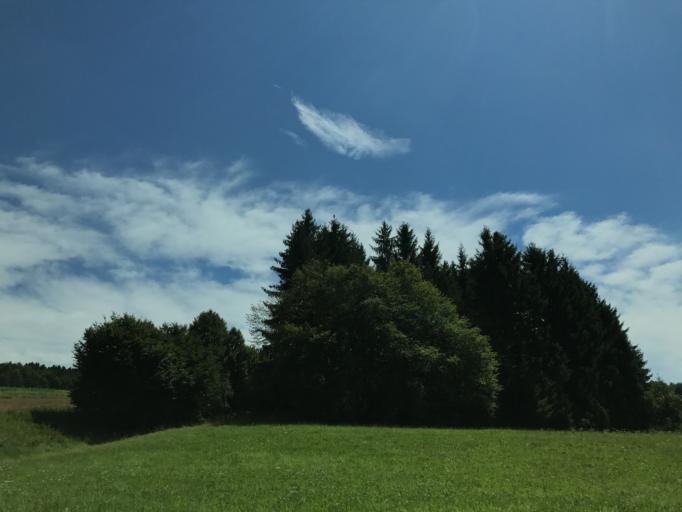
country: DE
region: Baden-Wuerttemberg
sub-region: Tuebingen Region
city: Langenenslingen
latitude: 48.1809
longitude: 9.3777
